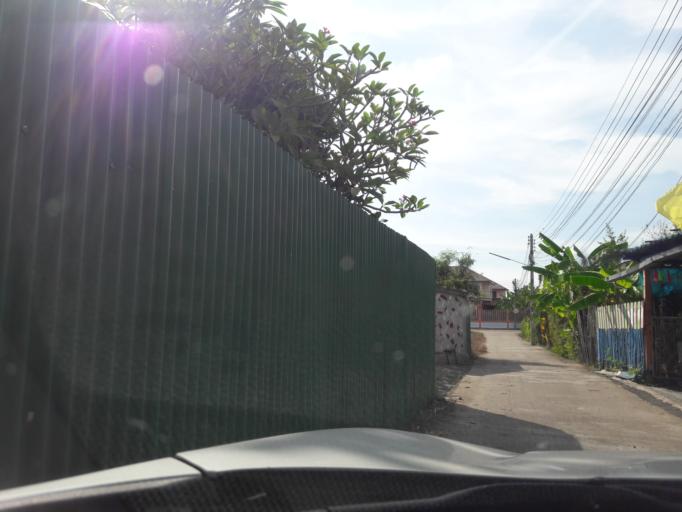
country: TH
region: Lop Buri
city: Ban Mi
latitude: 15.0428
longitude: 100.5332
